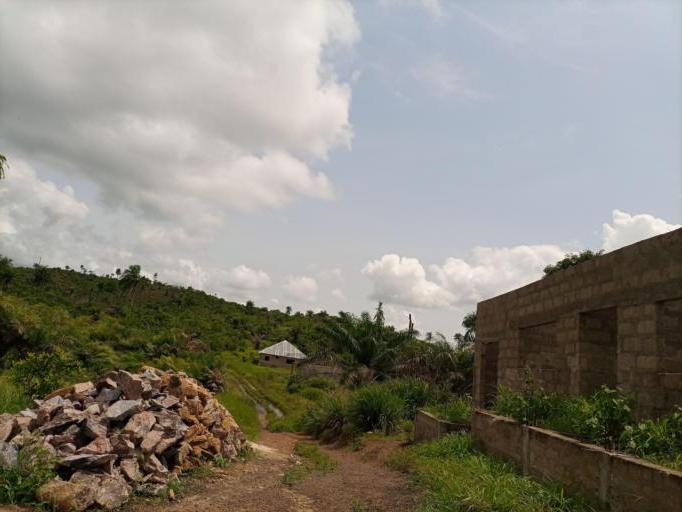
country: SL
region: Southern Province
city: Bo
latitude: 7.9792
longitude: -11.7701
